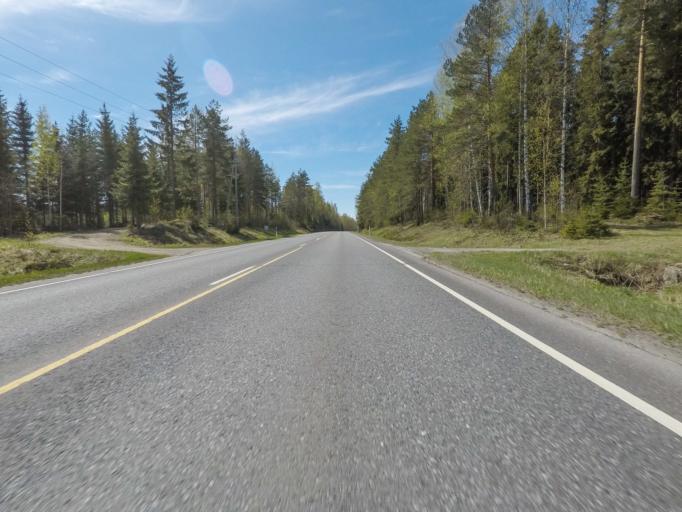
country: FI
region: Haeme
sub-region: Forssa
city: Humppila
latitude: 60.9831
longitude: 23.4429
